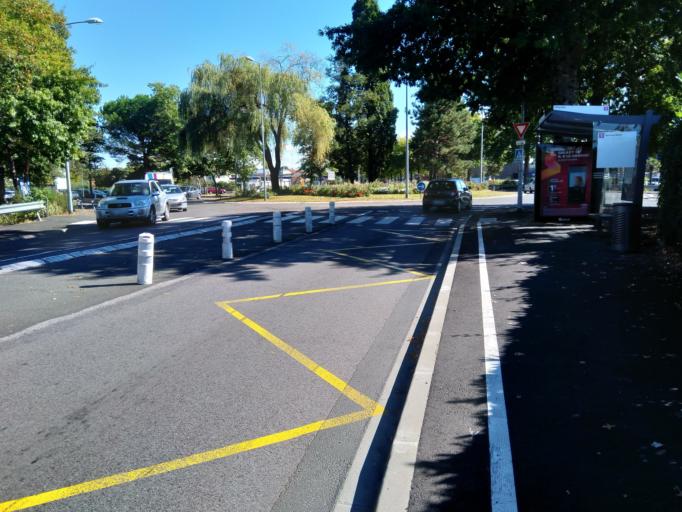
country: FR
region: Aquitaine
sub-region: Departement des Landes
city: Dax
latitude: 43.7107
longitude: -1.0424
